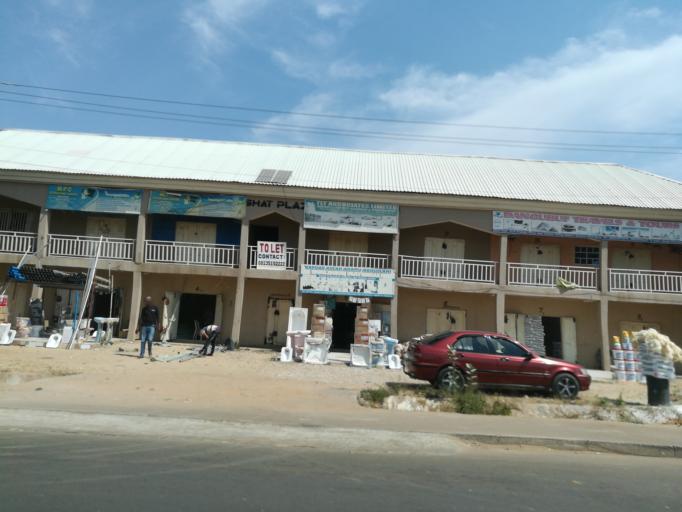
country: NG
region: Kano
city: Kano
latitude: 12.0215
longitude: 8.5175
